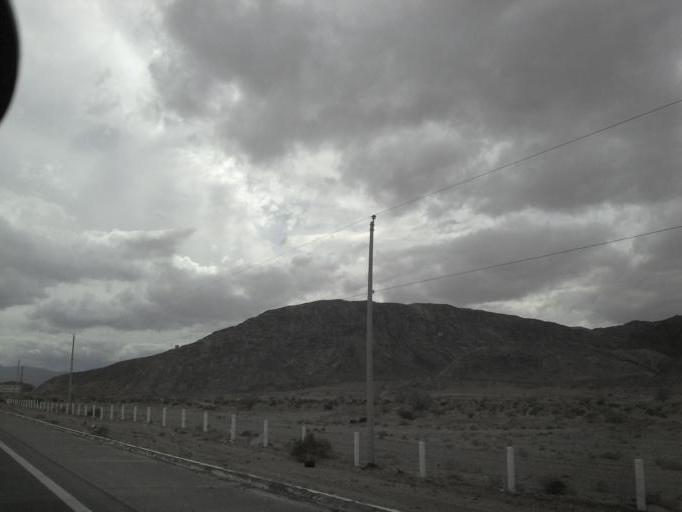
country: MX
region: Baja California
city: Progreso
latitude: 32.5847
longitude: -115.7112
